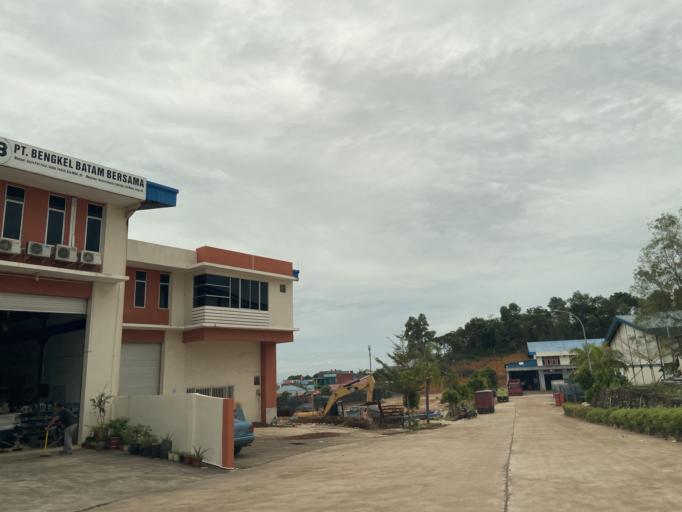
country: SG
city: Singapore
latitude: 1.1676
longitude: 104.0184
